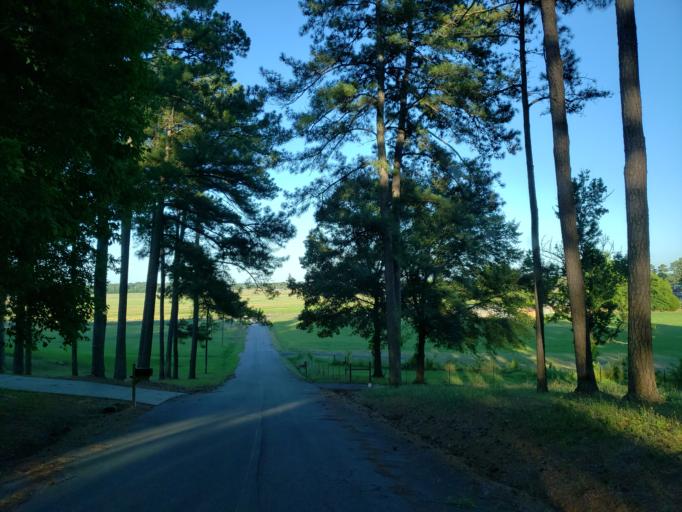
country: US
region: Georgia
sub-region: Polk County
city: Aragon
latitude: 34.0916
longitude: -84.9931
